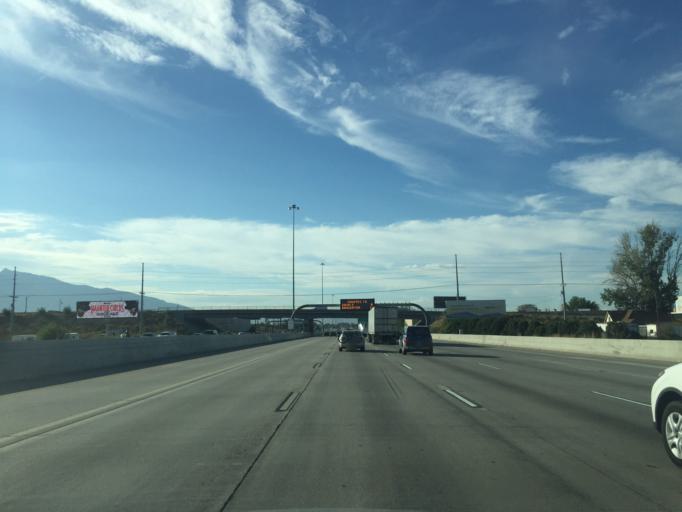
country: US
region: Utah
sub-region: Salt Lake County
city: Centerfield
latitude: 40.6884
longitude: -111.9032
